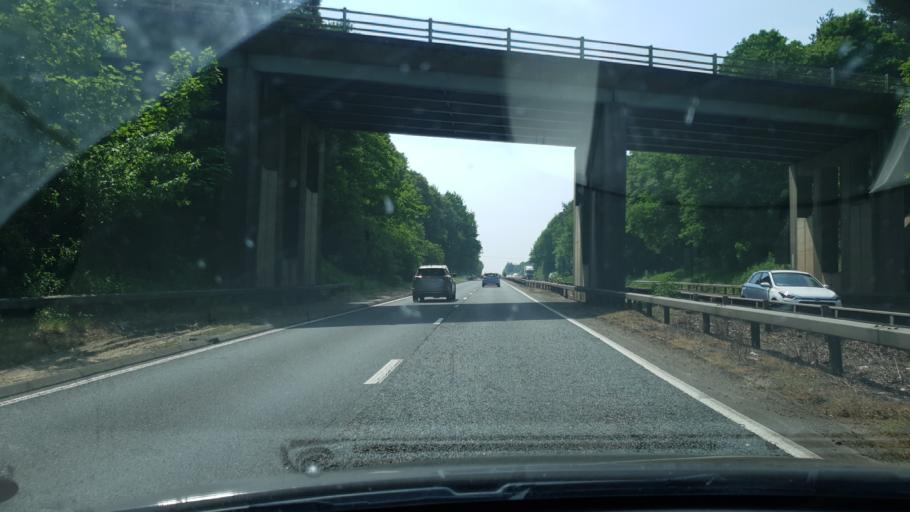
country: GB
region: England
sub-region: Suffolk
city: East Bergholt
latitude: 51.9571
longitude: 0.9684
